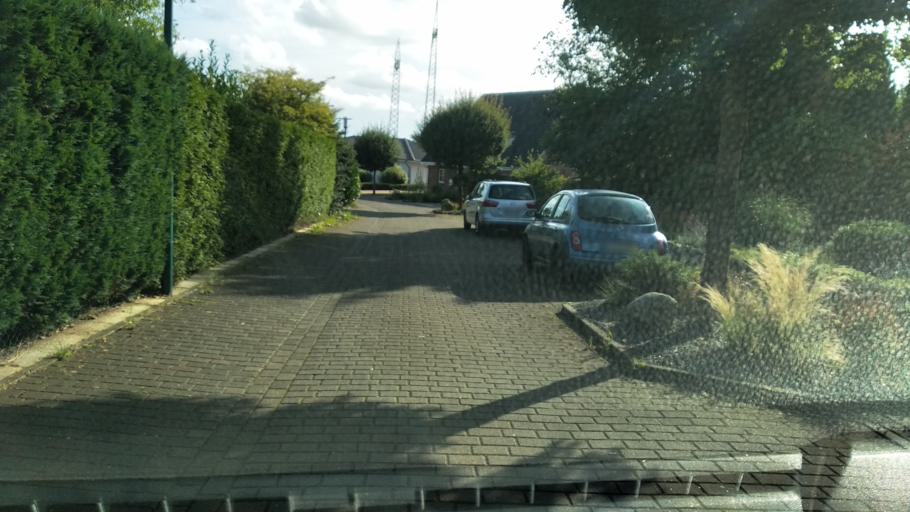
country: DE
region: Schleswig-Holstein
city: Busdorf
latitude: 54.4875
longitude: 9.5404
